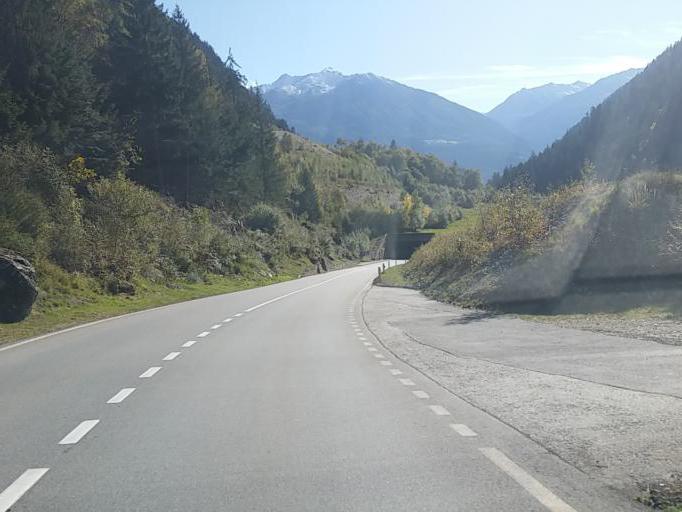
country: CH
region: Valais
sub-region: Leuk District
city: Gampel
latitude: 46.3536
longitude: 7.7580
